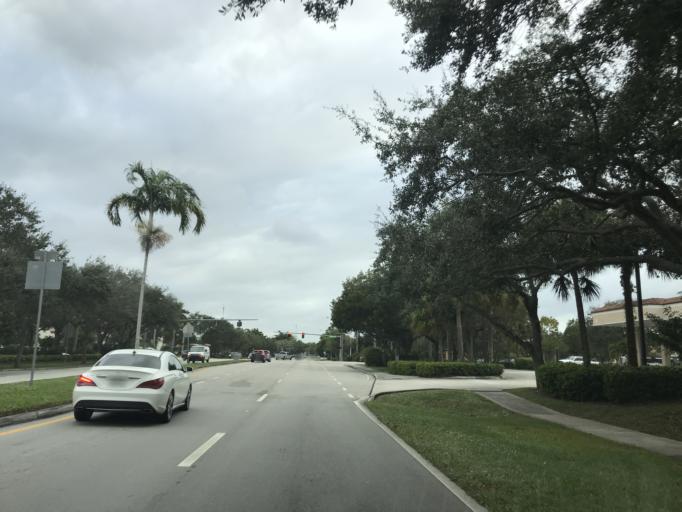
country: US
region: Florida
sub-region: Broward County
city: Parkland
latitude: 26.2985
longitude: -80.2493
